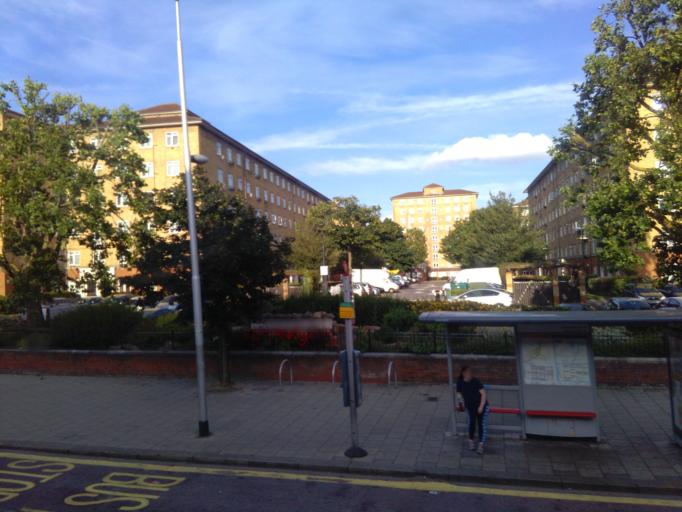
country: GB
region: England
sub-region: Greater London
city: Battersea
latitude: 51.4766
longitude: -0.1304
